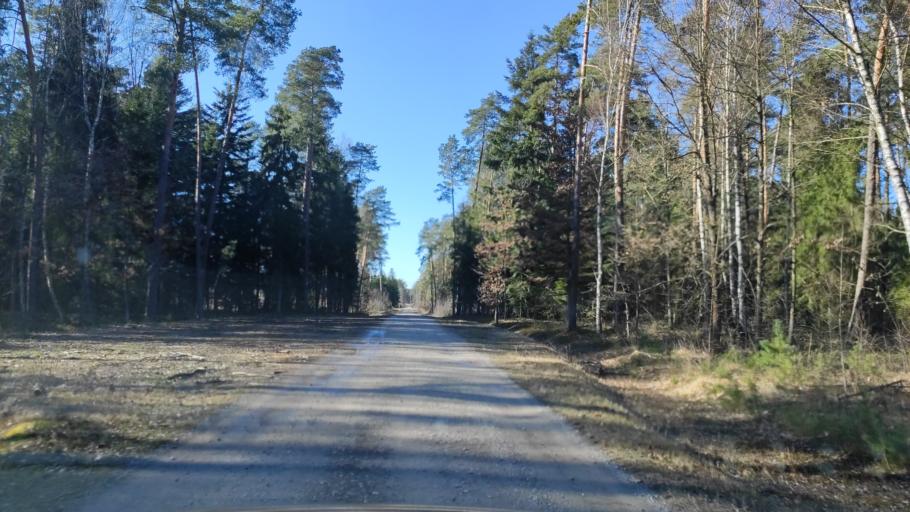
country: PL
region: Masovian Voivodeship
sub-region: Powiat radomski
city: Jedlnia-Letnisko
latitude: 51.4691
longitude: 21.3079
